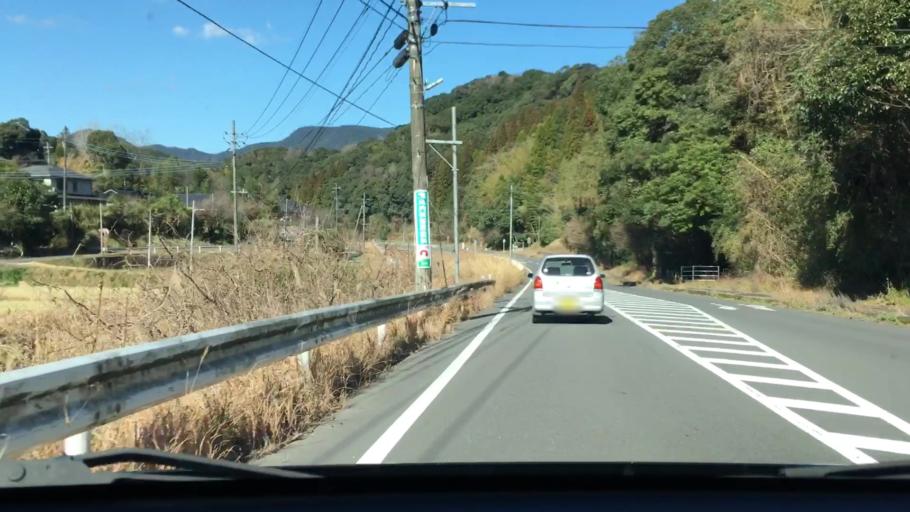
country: JP
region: Kagoshima
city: Ijuin
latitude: 31.6951
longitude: 130.4616
